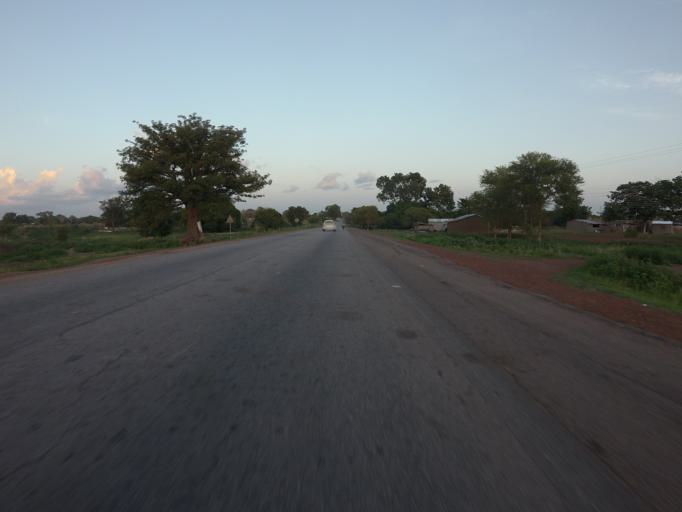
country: GH
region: Upper East
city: Navrongo
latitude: 10.8642
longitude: -1.0365
